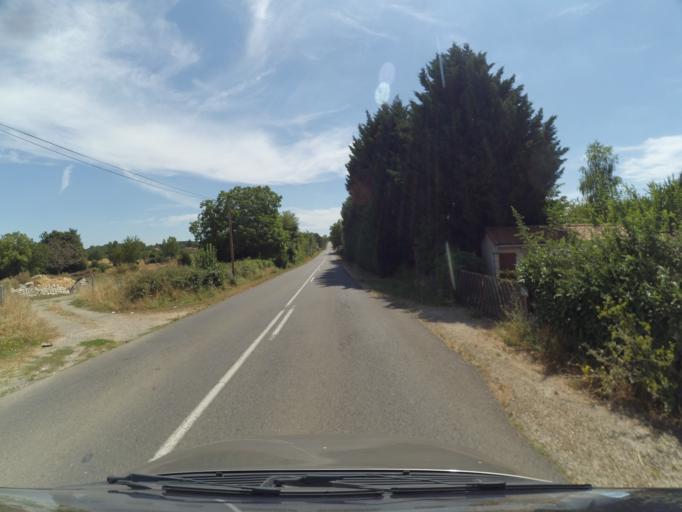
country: FR
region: Poitou-Charentes
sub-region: Departement de la Vienne
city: Usson-du-Poitou
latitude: 46.2711
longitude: 0.5194
